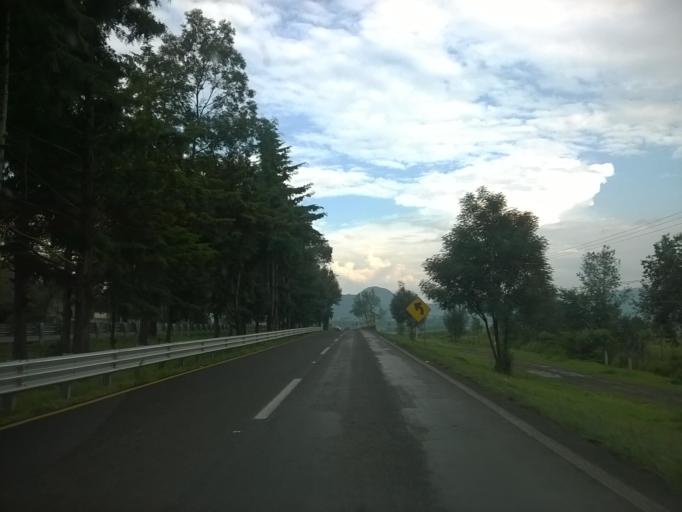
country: MX
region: Michoacan
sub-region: Huiramba
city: El Pedregal
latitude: 19.5306
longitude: -101.4831
